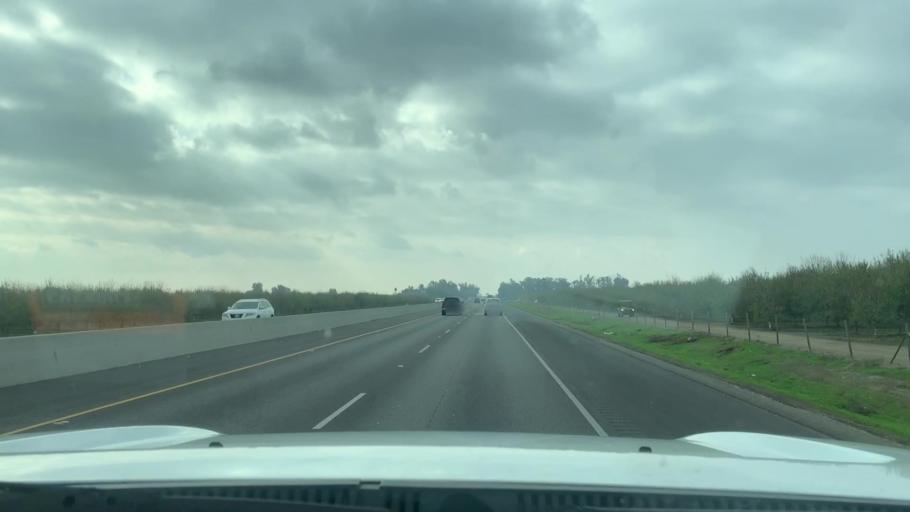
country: US
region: California
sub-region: Kings County
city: Armona
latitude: 36.3033
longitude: -119.7326
